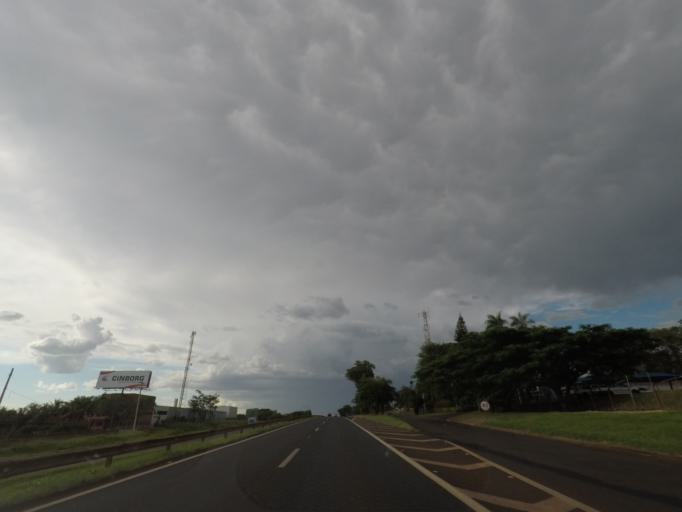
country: BR
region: Sao Paulo
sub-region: Jardinopolis
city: Jardinopolis
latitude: -21.0458
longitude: -47.8274
